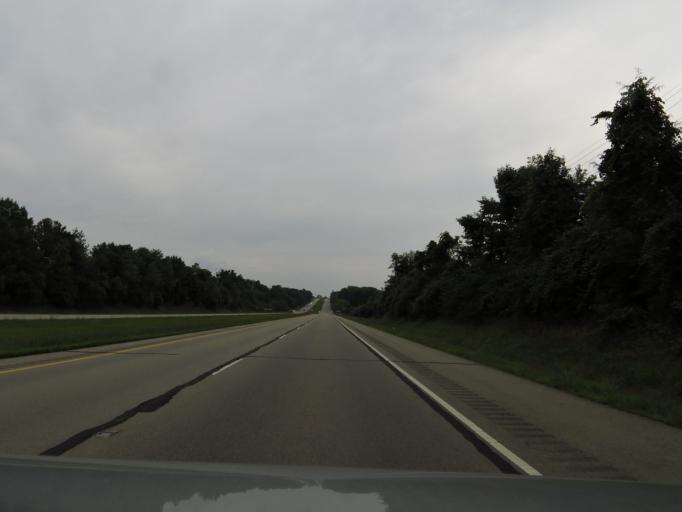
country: US
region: Ohio
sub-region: Brown County
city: Ripley
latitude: 38.7971
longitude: -83.7974
